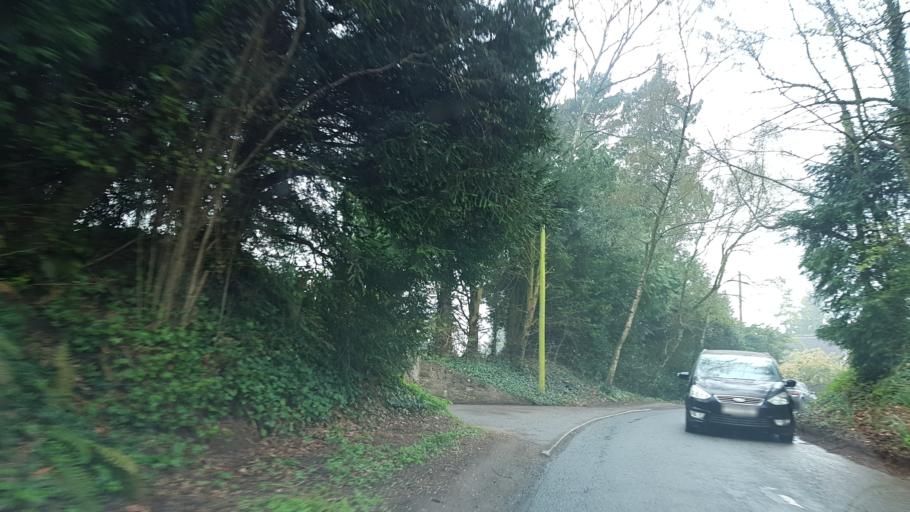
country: GB
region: England
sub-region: Herefordshire
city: Ledbury
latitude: 52.0640
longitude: -2.4210
